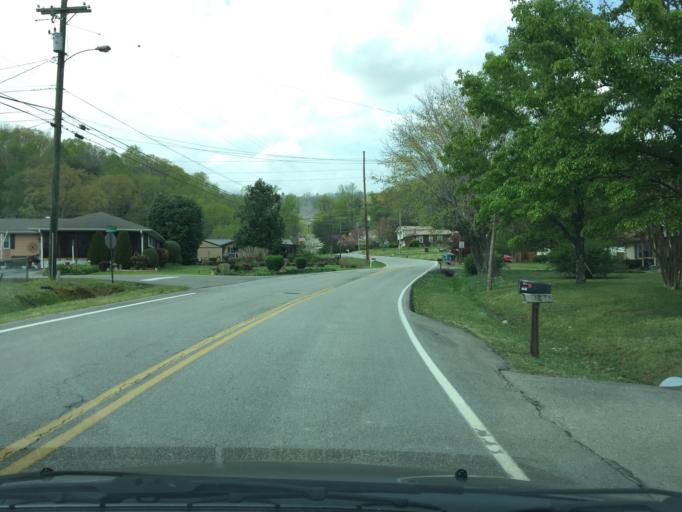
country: US
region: Tennessee
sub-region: Hamilton County
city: Red Bank
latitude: 35.1392
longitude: -85.2842
